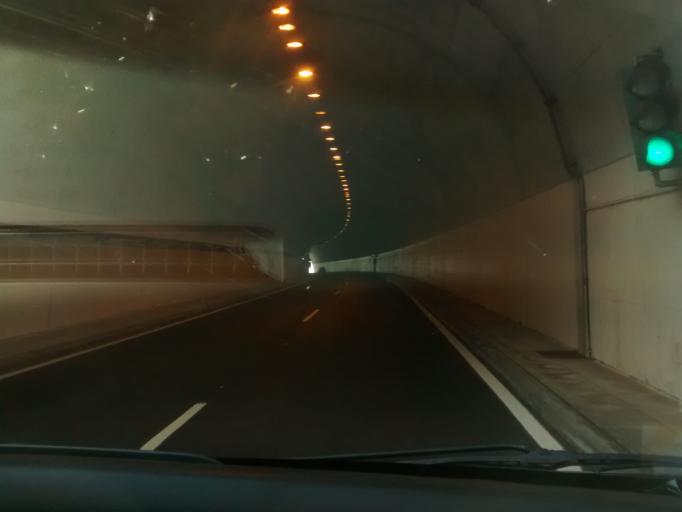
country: PT
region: Madeira
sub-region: Ribeira Brava
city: Campanario
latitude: 32.6809
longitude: -17.0576
